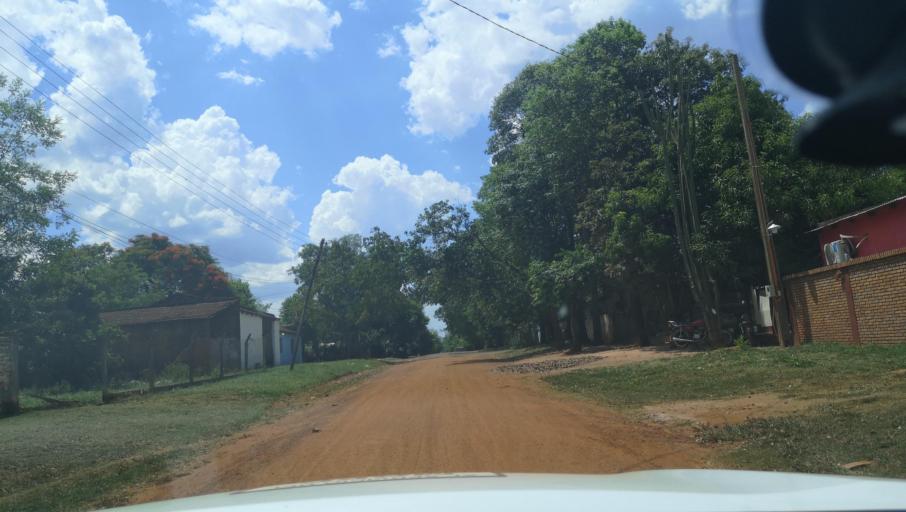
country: PY
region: Itapua
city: Carmen del Parana
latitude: -27.1699
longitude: -56.2463
